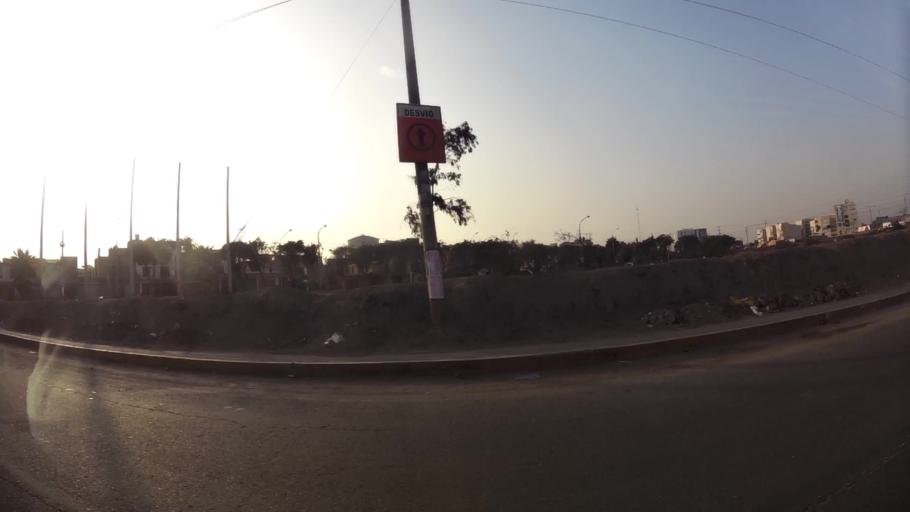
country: PE
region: Lima
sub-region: Lima
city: Independencia
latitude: -11.9627
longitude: -77.0699
